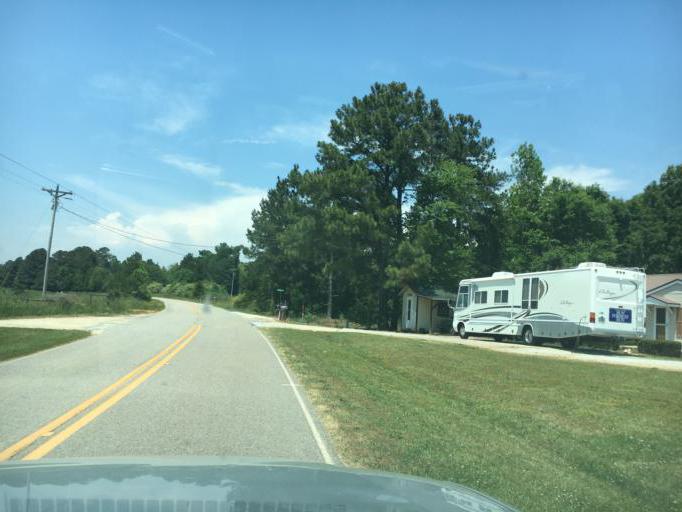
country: US
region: Georgia
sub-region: Hart County
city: Royston
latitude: 34.3038
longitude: -83.0943
